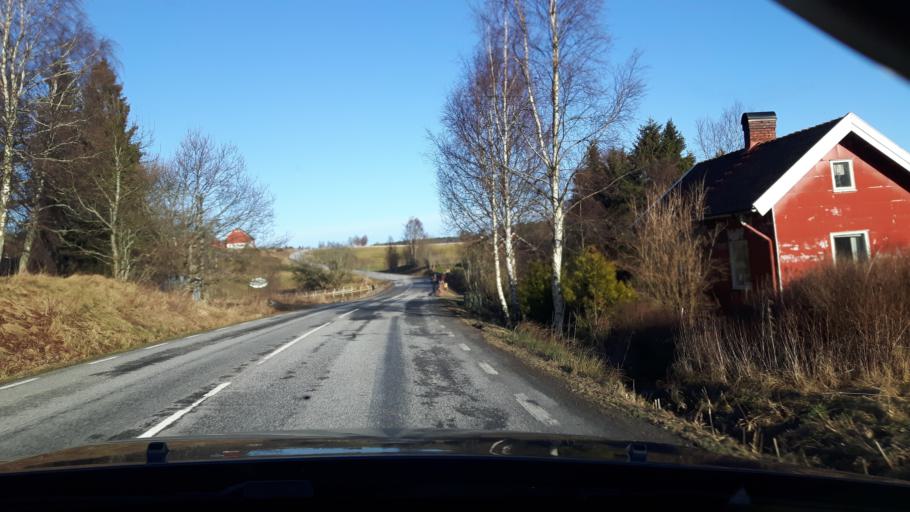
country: SE
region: Vaestra Goetaland
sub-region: Munkedals Kommun
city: Munkedal
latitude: 58.6282
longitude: 11.7732
